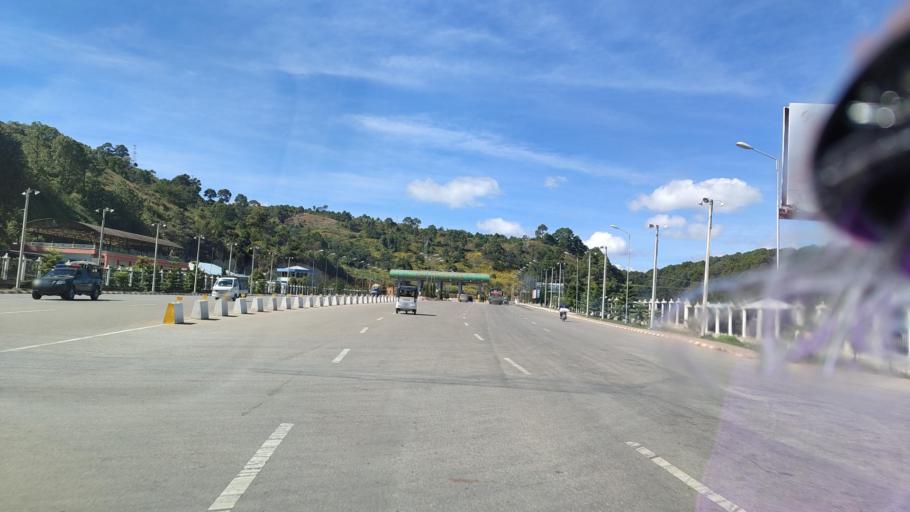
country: MM
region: Shan
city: Taunggyi
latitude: 20.6448
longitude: 96.6042
